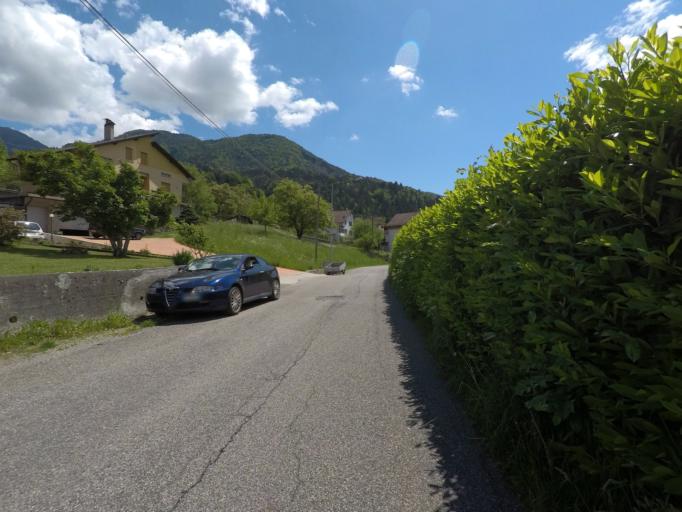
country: IT
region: Friuli Venezia Giulia
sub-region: Provincia di Udine
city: Ovaro
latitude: 46.4819
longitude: 12.8674
